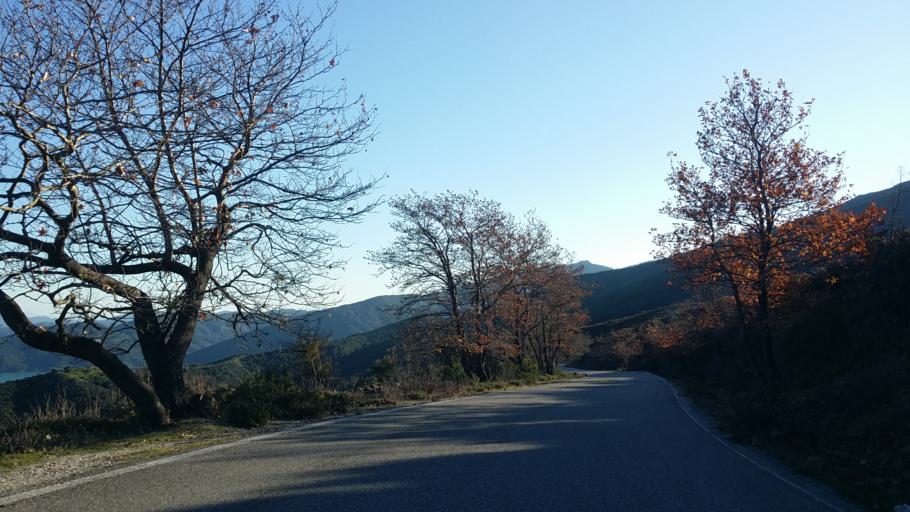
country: GR
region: West Greece
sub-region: Nomos Aitolias kai Akarnanias
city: Sardinia
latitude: 38.8470
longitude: 21.3169
